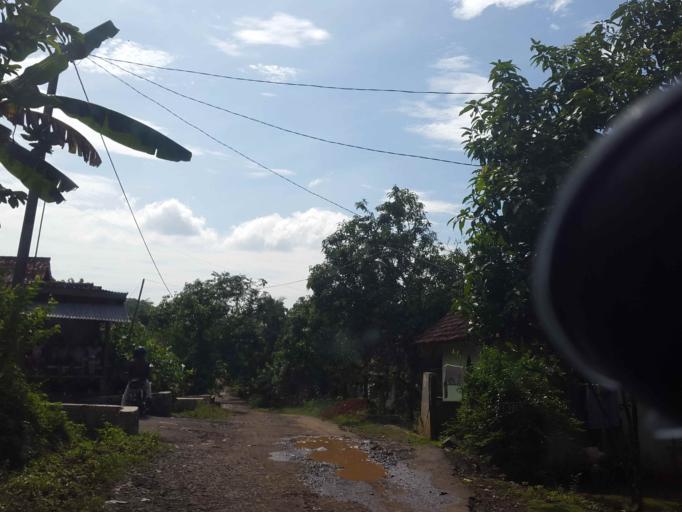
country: ID
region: Central Java
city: Garbi
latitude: -7.4579
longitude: 109.1914
